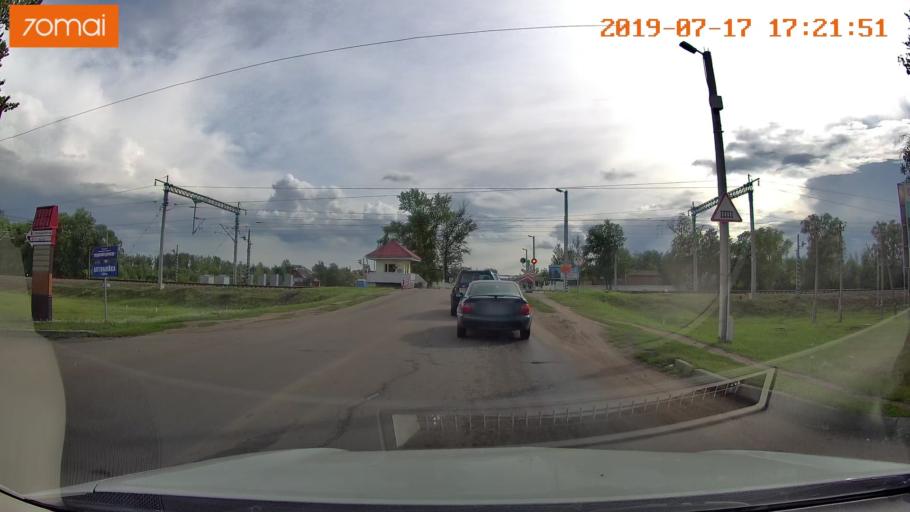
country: BY
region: Mogilev
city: Babruysk
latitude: 53.1466
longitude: 29.1773
